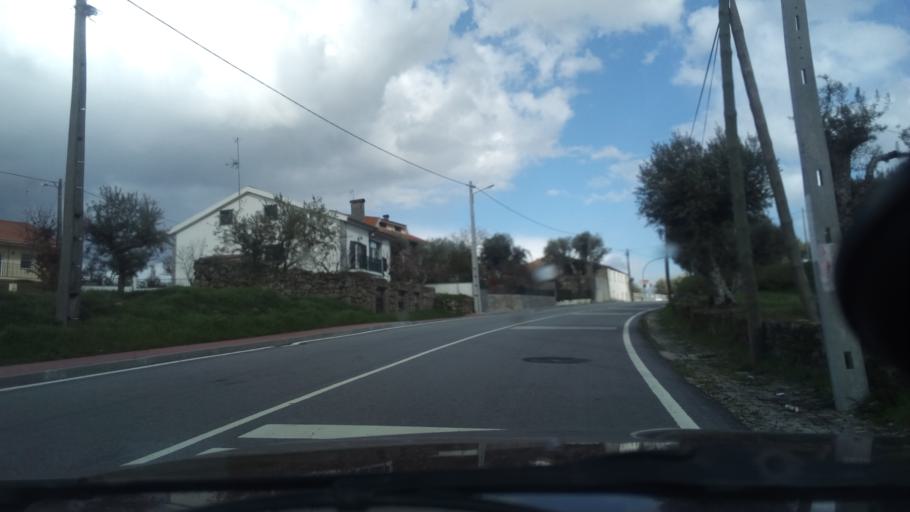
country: PT
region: Guarda
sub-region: Celorico da Beira
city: Celorico da Beira
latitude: 40.6401
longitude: -7.3566
